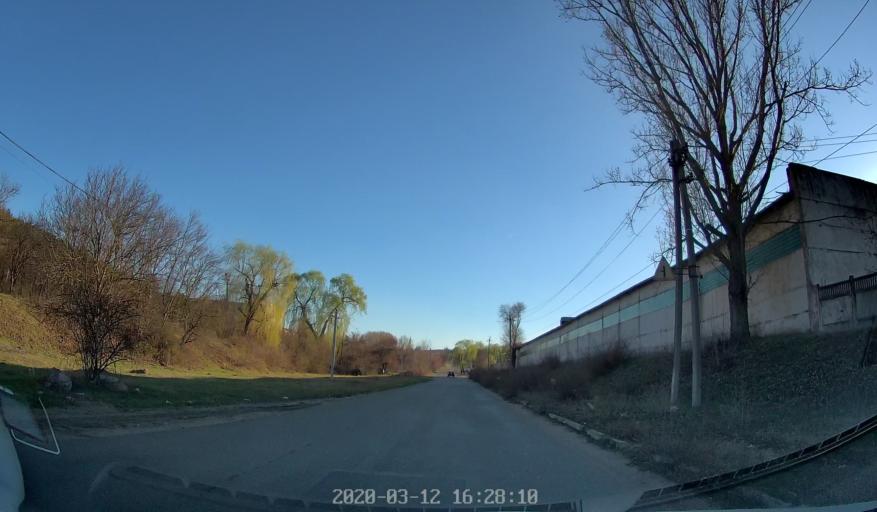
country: MD
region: Anenii Noi
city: Anenii Noi
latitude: 46.8702
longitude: 29.2259
